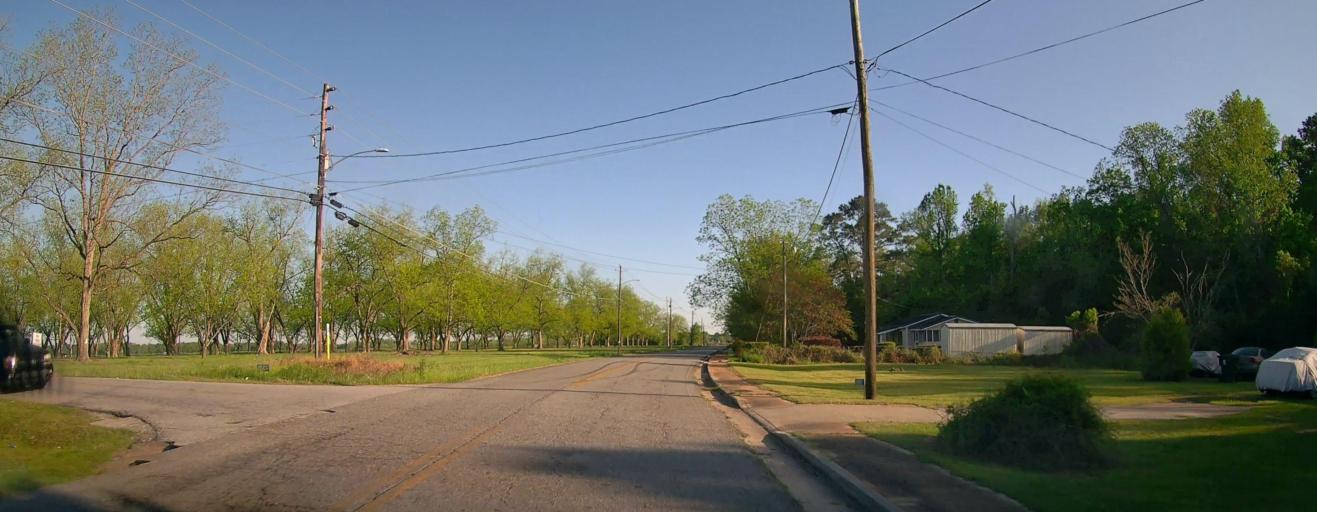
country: US
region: Georgia
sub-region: Macon County
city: Oglethorpe
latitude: 32.2902
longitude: -84.0581
